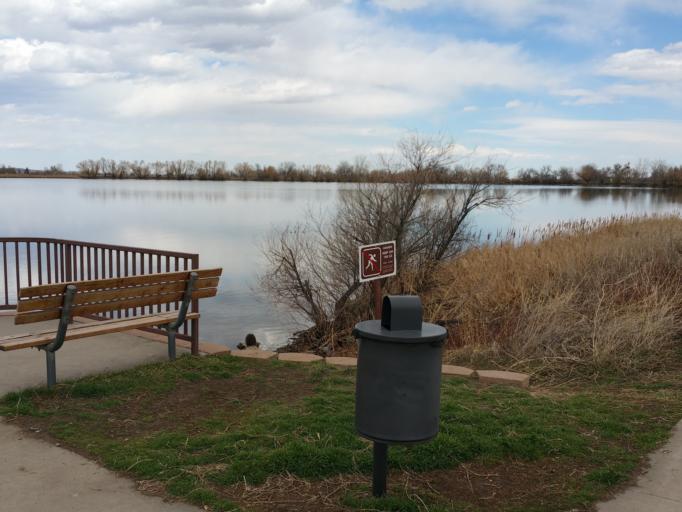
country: US
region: Colorado
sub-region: Jefferson County
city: Wheat Ridge
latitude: 39.7556
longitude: -105.1028
